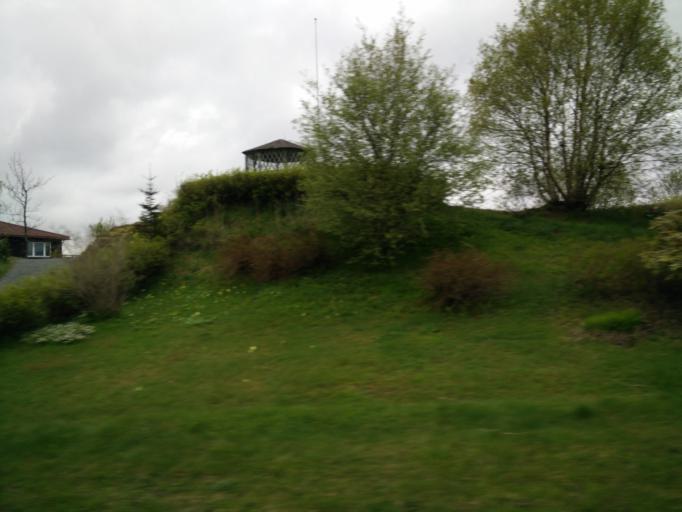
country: NO
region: Sor-Trondelag
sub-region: Skaun
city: Borsa
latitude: 63.3199
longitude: 10.1418
